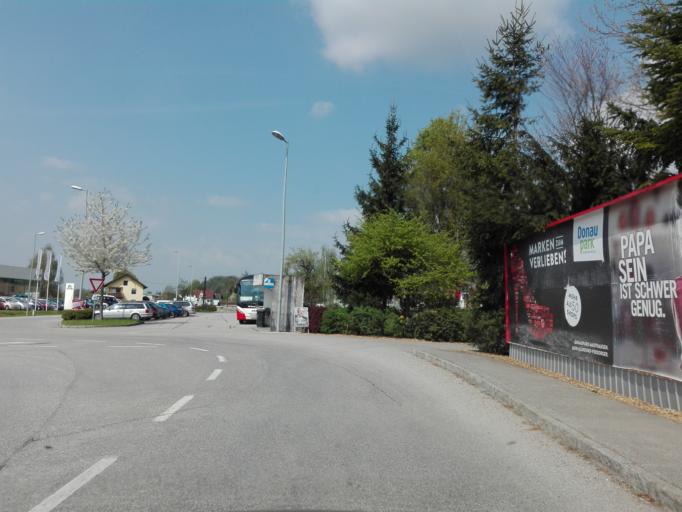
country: AT
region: Upper Austria
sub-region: Politischer Bezirk Perg
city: Perg
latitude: 48.2295
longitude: 14.7002
